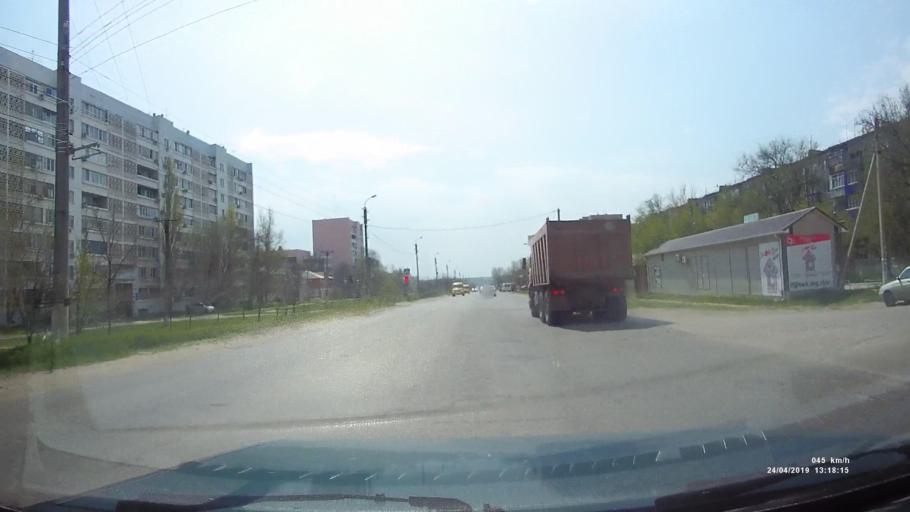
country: RU
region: Kalmykiya
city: Elista
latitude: 46.3031
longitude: 44.2952
